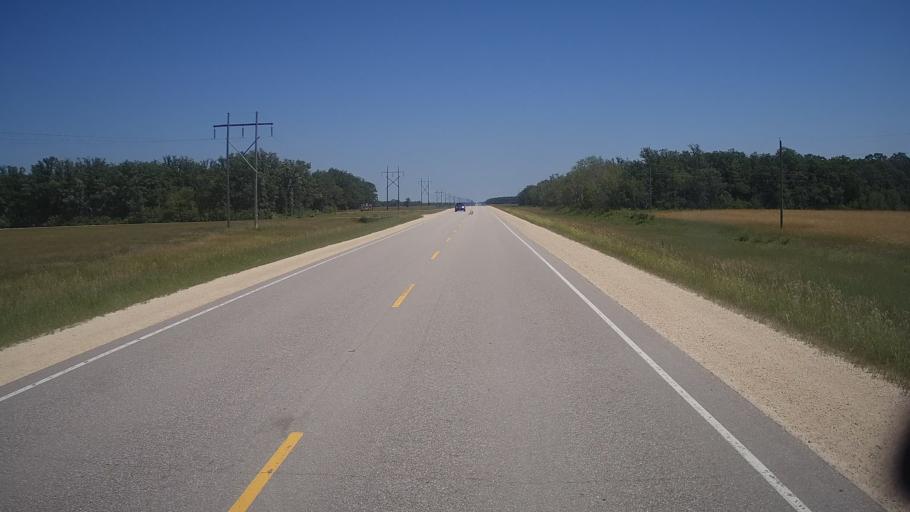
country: CA
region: Manitoba
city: Stonewall
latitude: 50.1228
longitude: -97.4787
